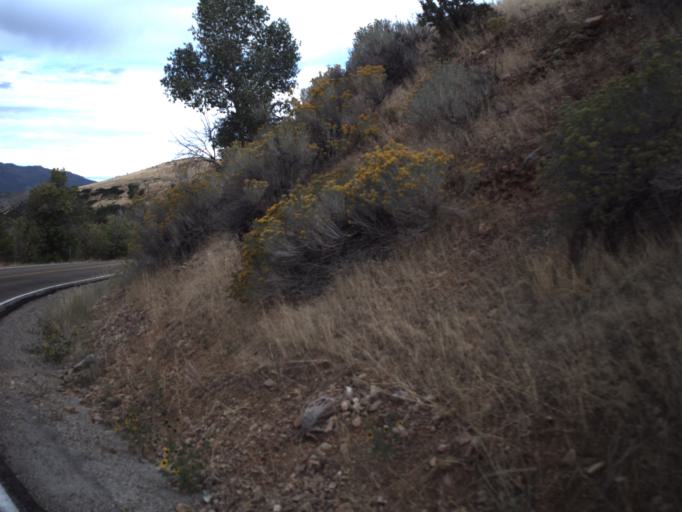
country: US
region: Utah
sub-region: Morgan County
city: Morgan
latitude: 40.9379
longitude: -111.6408
